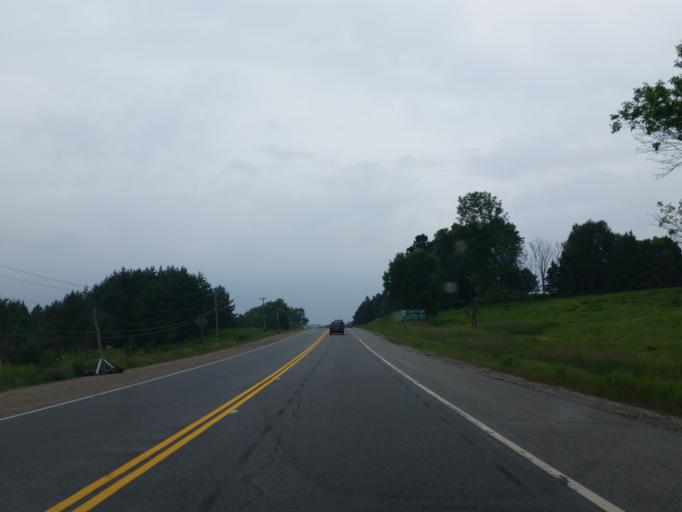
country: CA
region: Ontario
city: Huntsville
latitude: 45.3550
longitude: -79.0914
